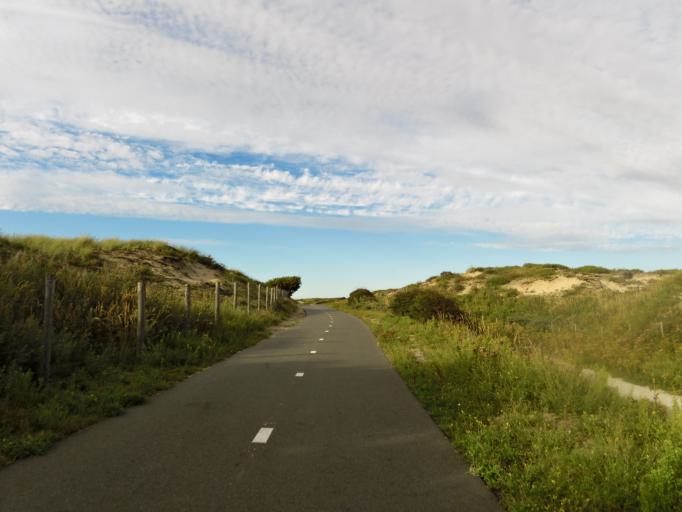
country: NL
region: South Holland
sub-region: Gemeente Noordwijk
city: Noordwijk-Binnen
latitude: 52.2275
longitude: 4.4162
